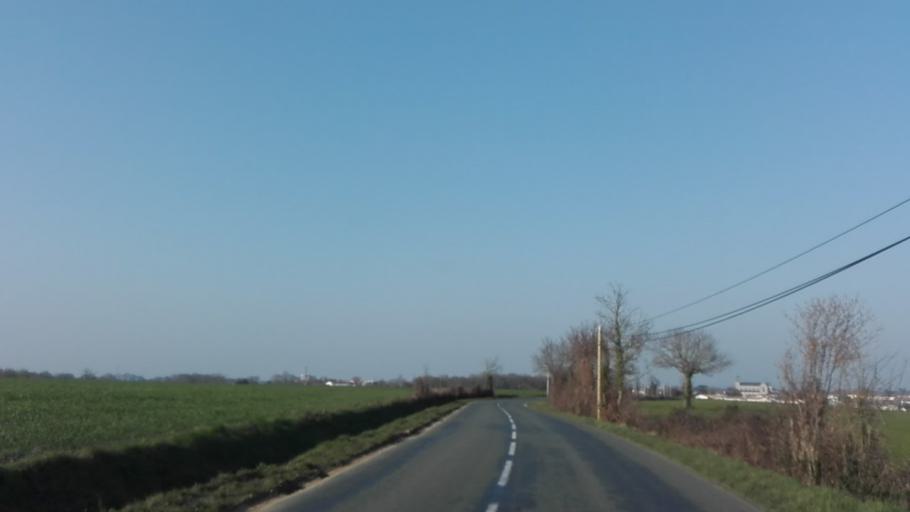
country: FR
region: Pays de la Loire
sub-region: Departement de la Vendee
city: Saint-Georges-de-Montaigu
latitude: 46.9387
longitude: -1.3027
